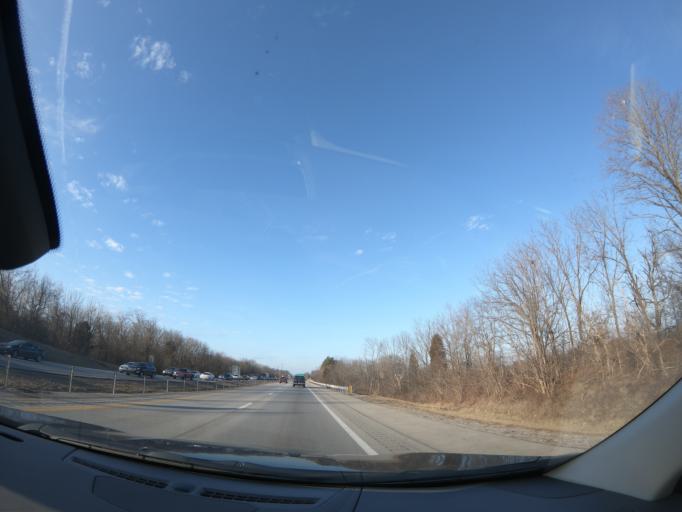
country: US
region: Kentucky
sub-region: Jefferson County
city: Middletown
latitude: 38.2143
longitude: -85.5063
